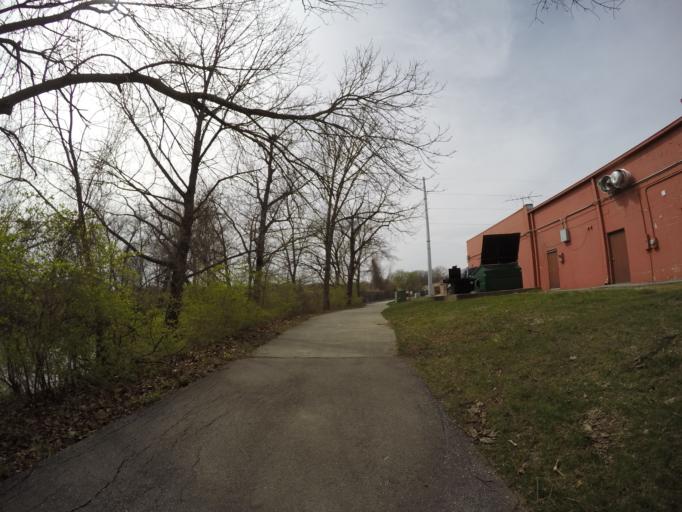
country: US
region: Kansas
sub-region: Johnson County
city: Leawood
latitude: 38.9409
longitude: -94.6061
